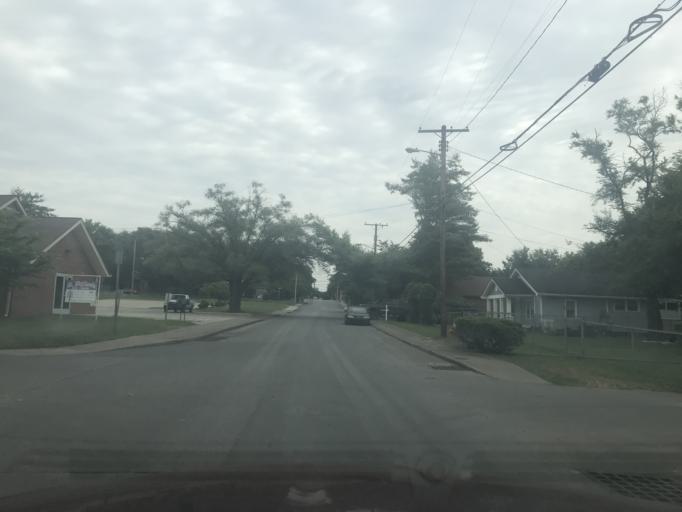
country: US
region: Tennessee
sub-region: Davidson County
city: Nashville
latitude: 36.1763
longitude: -86.8165
